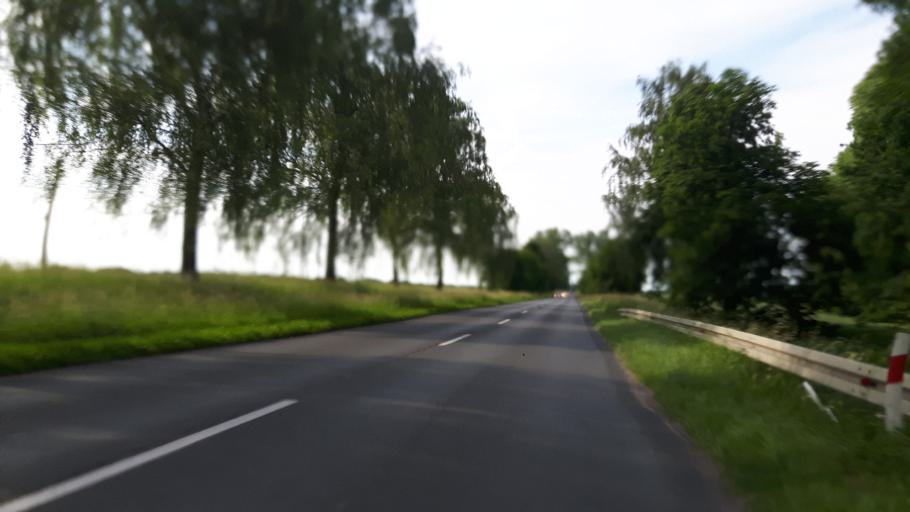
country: PL
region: West Pomeranian Voivodeship
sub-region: Powiat gryficki
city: Gryfice
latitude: 53.8925
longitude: 15.2070
